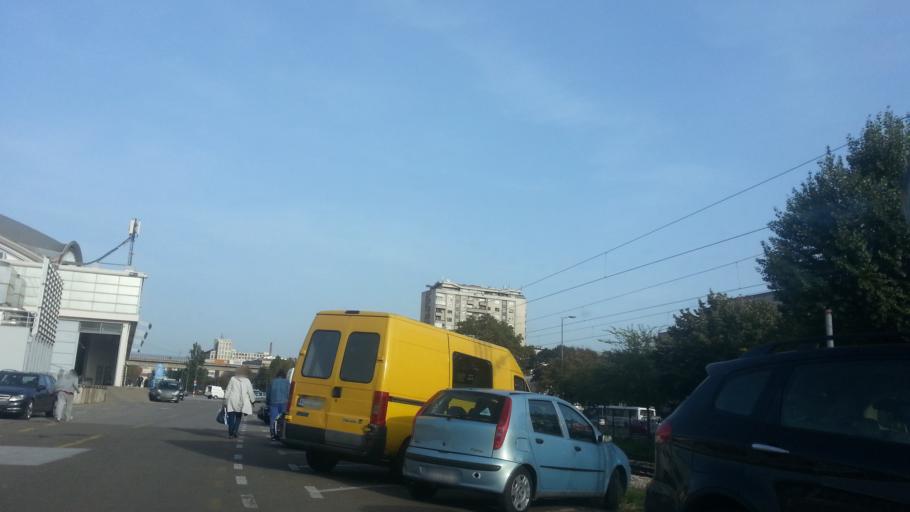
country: RS
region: Central Serbia
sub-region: Belgrade
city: Novi Beograd
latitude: 44.7952
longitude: 20.4349
